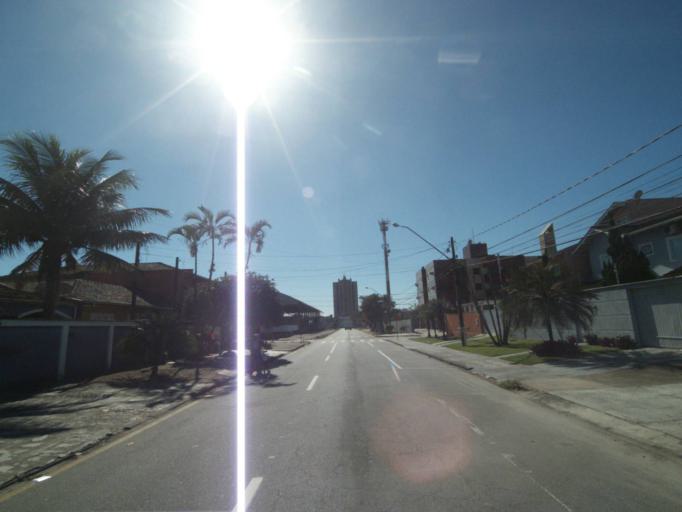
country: BR
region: Parana
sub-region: Paranagua
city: Paranagua
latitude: -25.5228
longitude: -48.5194
